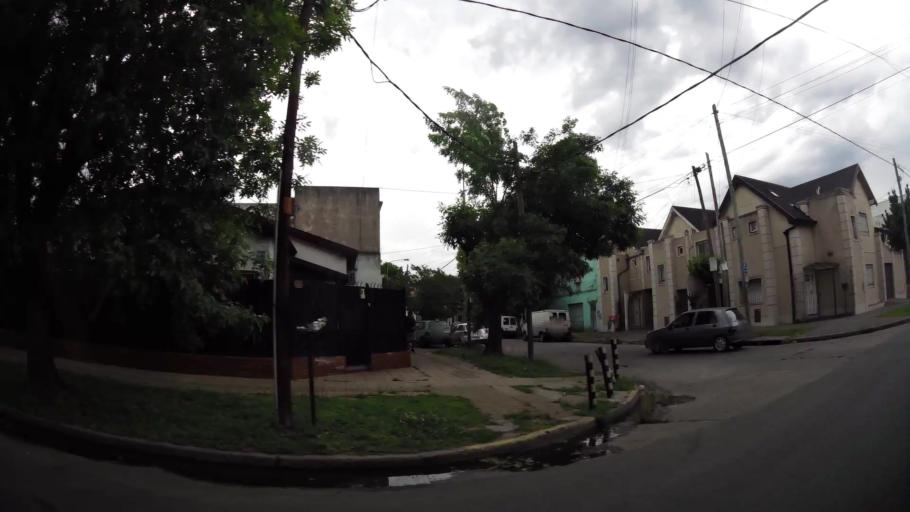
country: AR
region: Buenos Aires
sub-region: Partido de Lanus
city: Lanus
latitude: -34.6875
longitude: -58.3905
